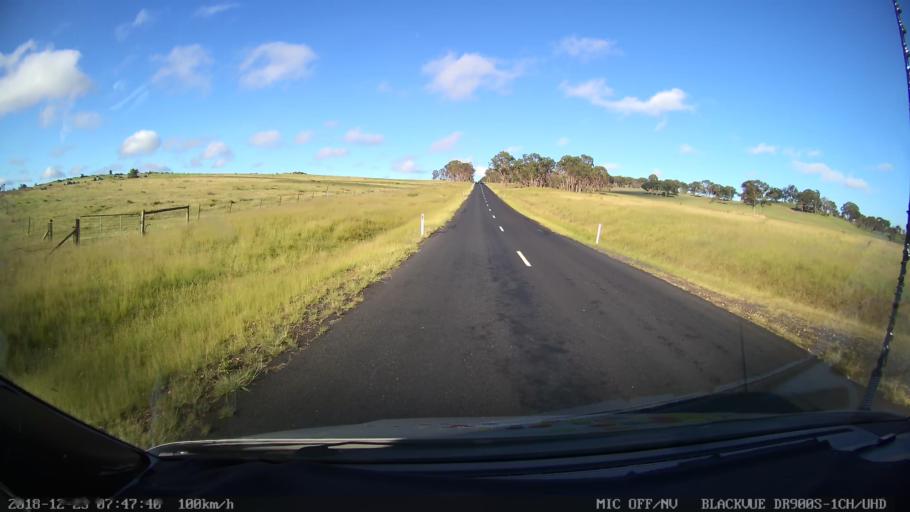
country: AU
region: New South Wales
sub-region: Armidale Dumaresq
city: Armidale
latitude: -30.5280
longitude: 151.8973
